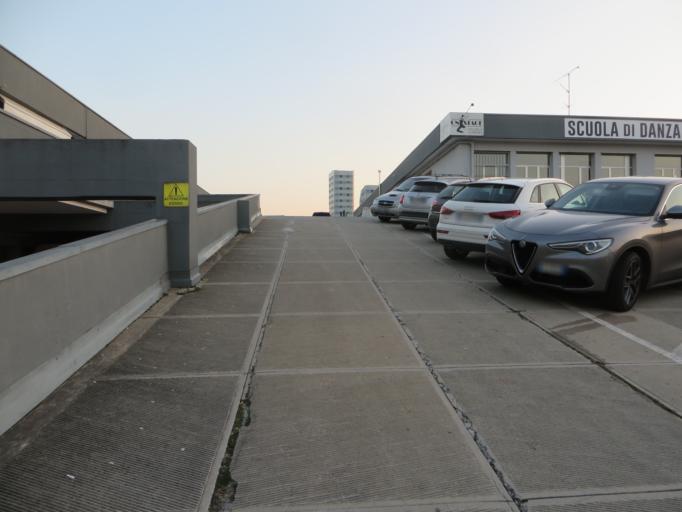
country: IT
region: Lombardy
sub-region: Provincia di Brescia
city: Bovezzo
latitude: 45.5776
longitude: 10.2292
